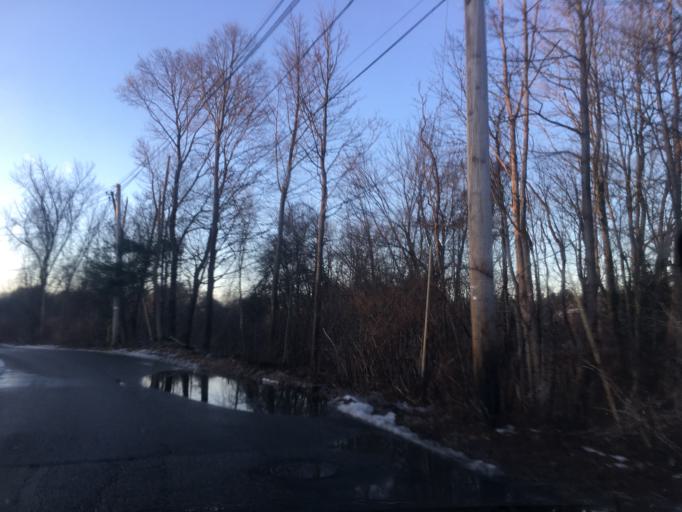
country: US
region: Massachusetts
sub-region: Middlesex County
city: Billerica
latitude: 42.5473
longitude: -71.2749
